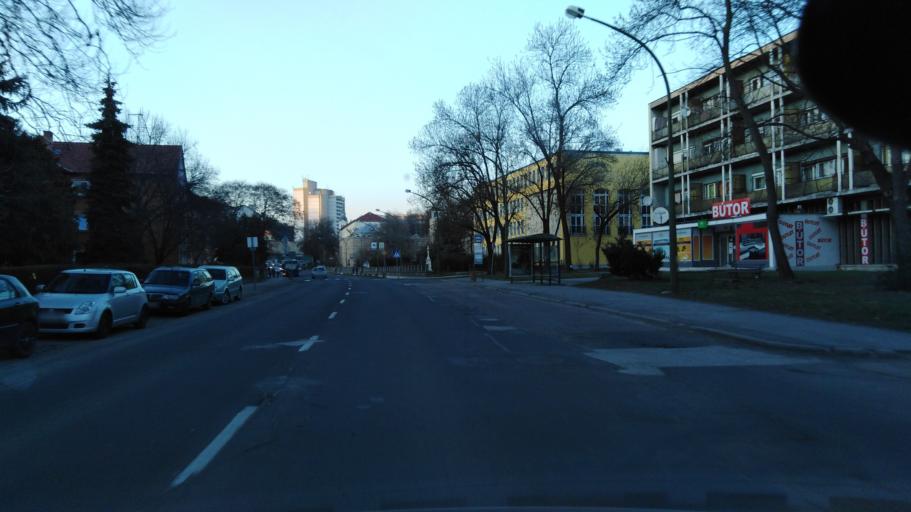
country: HU
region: Nograd
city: Salgotarjan
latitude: 48.0986
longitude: 19.8054
